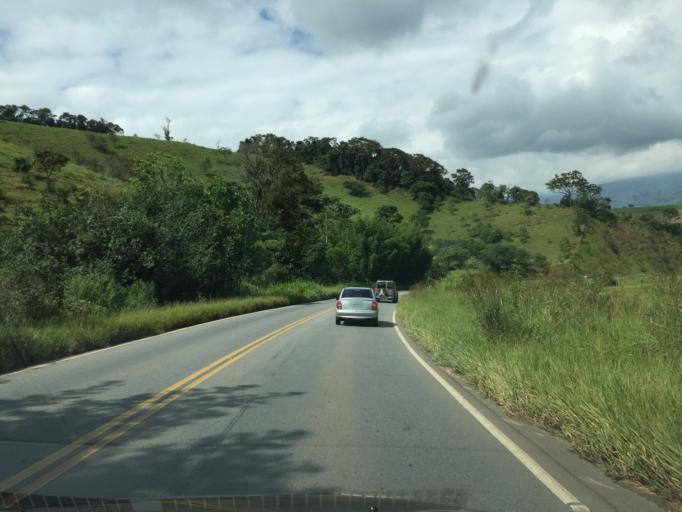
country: BR
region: Minas Gerais
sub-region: Itanhandu
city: Itanhandu
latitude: -22.3256
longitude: -44.9325
